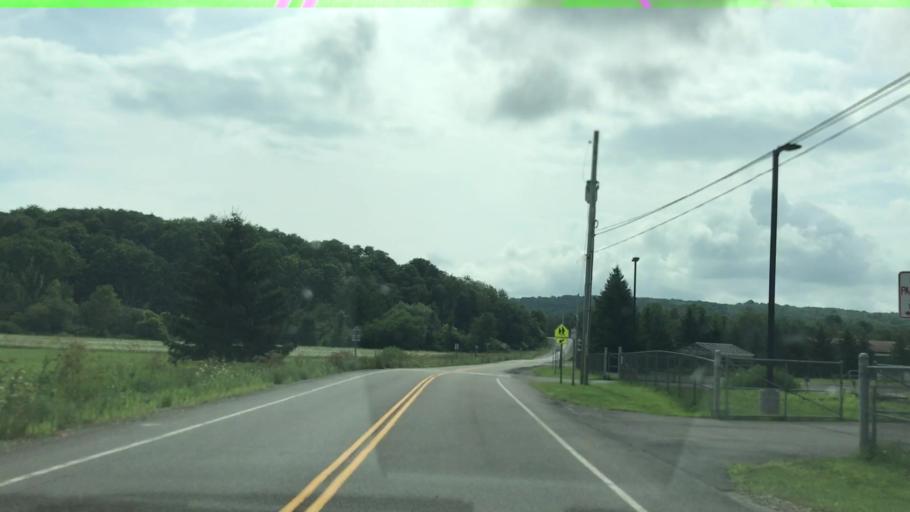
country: US
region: New York
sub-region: Ontario County
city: Naples
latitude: 42.5101
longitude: -77.2774
